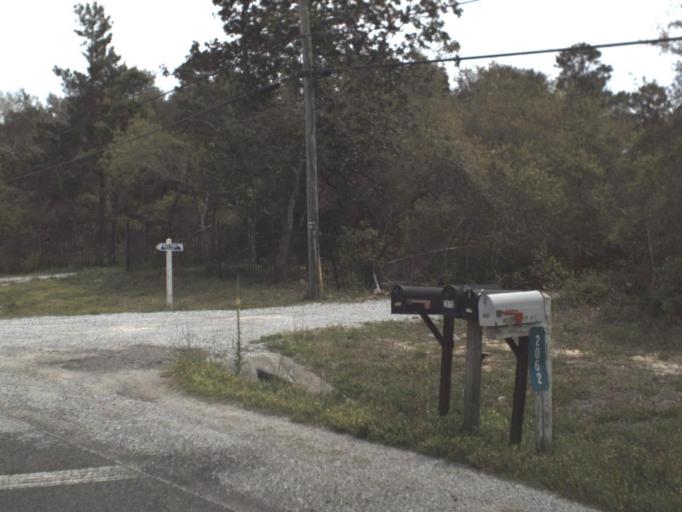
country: US
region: Florida
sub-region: Santa Rosa County
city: Navarre
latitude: 30.4095
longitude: -86.8171
